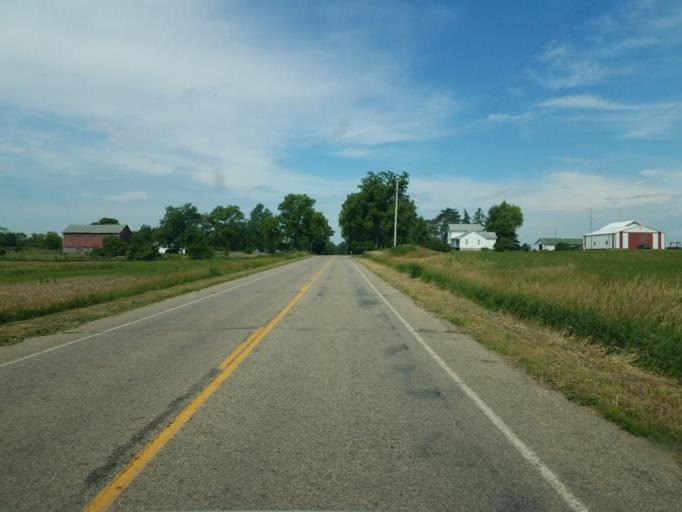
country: US
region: Michigan
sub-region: Barry County
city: Nashville
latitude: 42.6260
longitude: -84.9811
